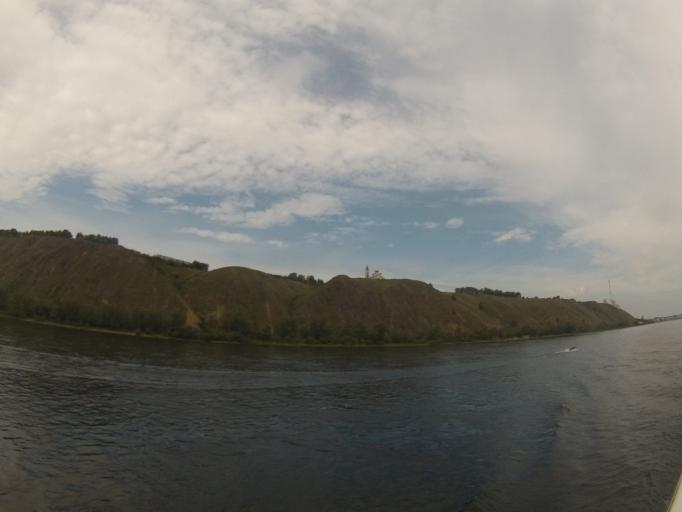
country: RU
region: Krasnoyarskiy
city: Krasnoyarsk
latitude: 55.9791
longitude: 92.7644
